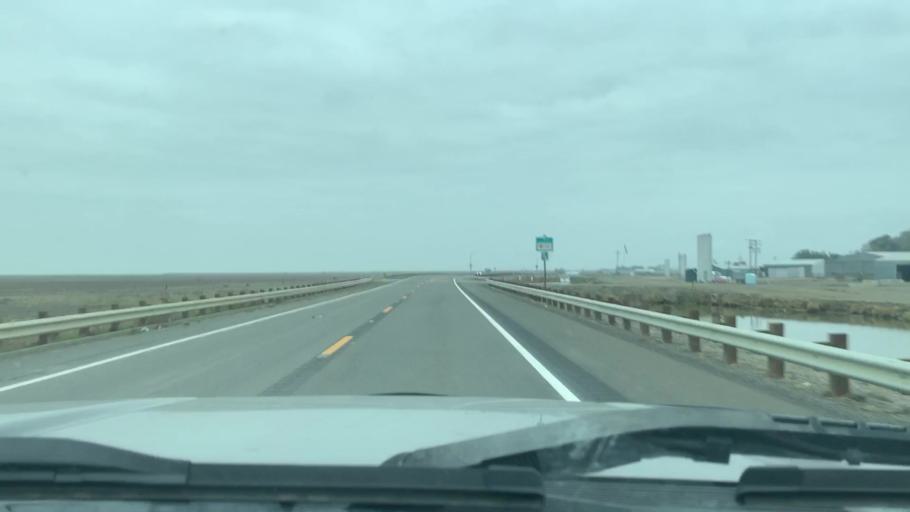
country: US
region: California
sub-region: Kings County
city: Stratford
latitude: 36.1210
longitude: -119.8937
